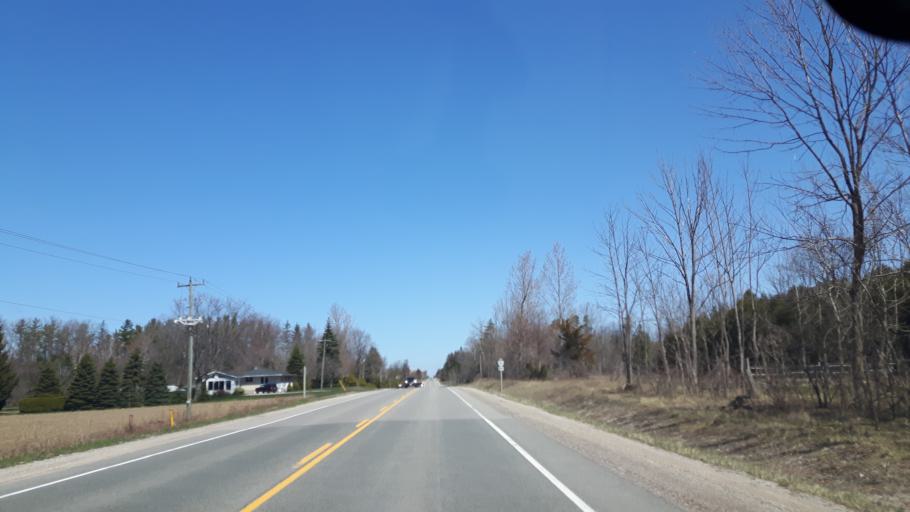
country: CA
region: Ontario
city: Goderich
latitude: 43.6632
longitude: -81.7056
